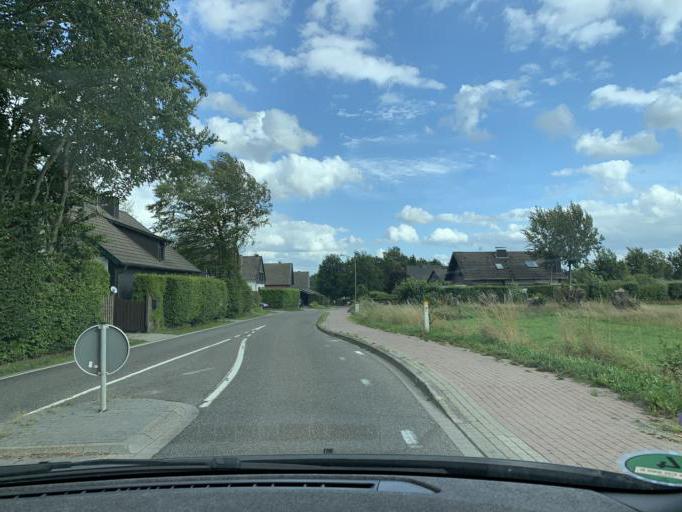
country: DE
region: North Rhine-Westphalia
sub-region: Regierungsbezirk Koln
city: Monschau
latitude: 50.5929
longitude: 6.2463
